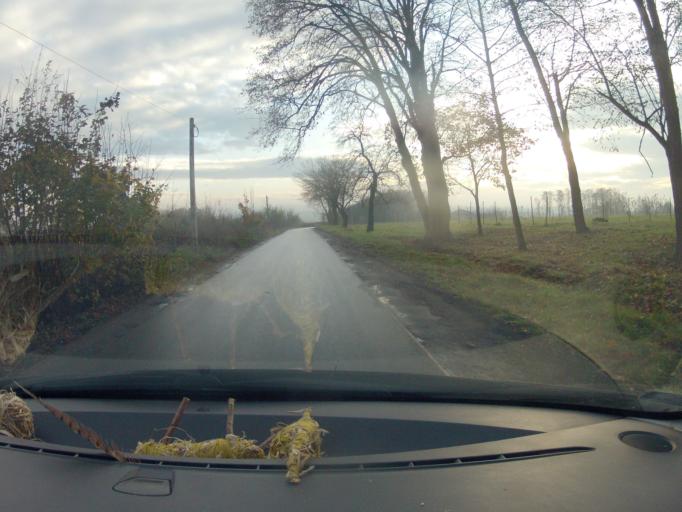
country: PL
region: Lesser Poland Voivodeship
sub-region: Krakow
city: Sidzina
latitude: 50.0008
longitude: 19.8871
